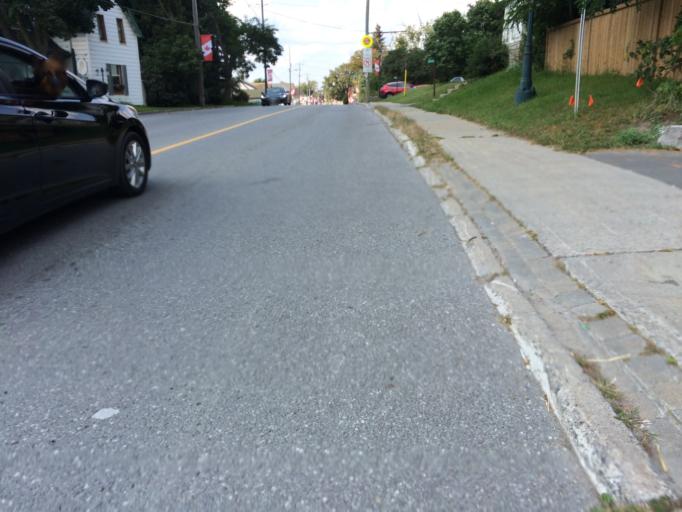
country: CA
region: Ontario
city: Bells Corners
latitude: 45.2232
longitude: -75.6810
